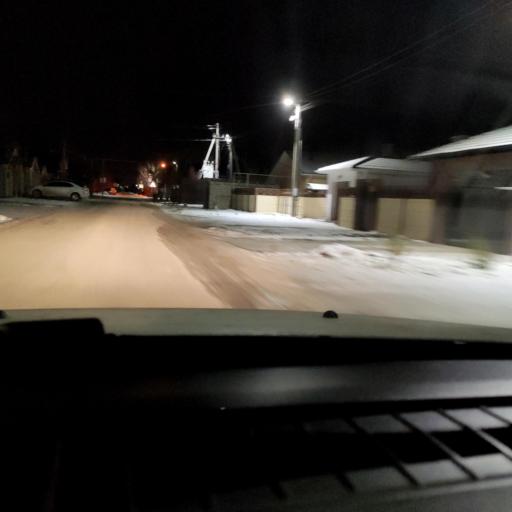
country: RU
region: Samara
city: Podstepki
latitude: 53.5107
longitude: 49.1743
